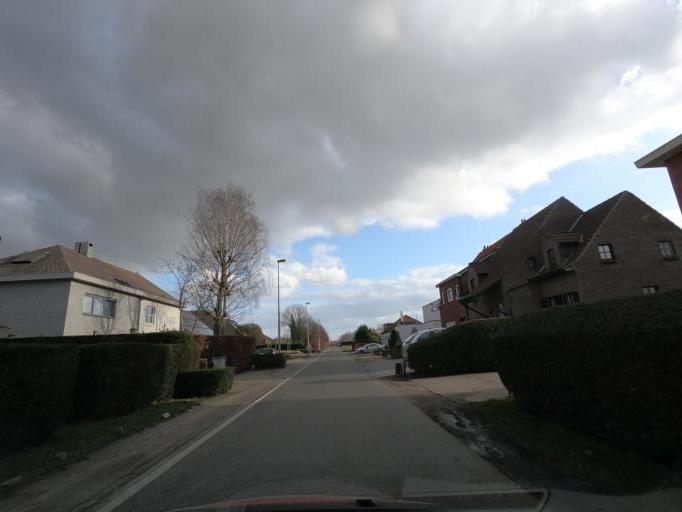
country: BE
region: Flanders
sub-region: Provincie Antwerpen
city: Wommelgem
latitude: 51.1841
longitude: 4.5084
